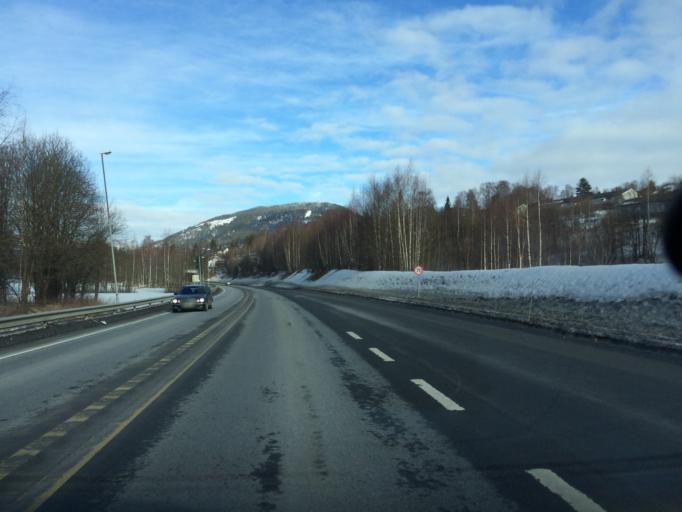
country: NO
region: Oppland
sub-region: Lillehammer
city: Lillehammer
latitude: 61.1182
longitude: 10.4461
